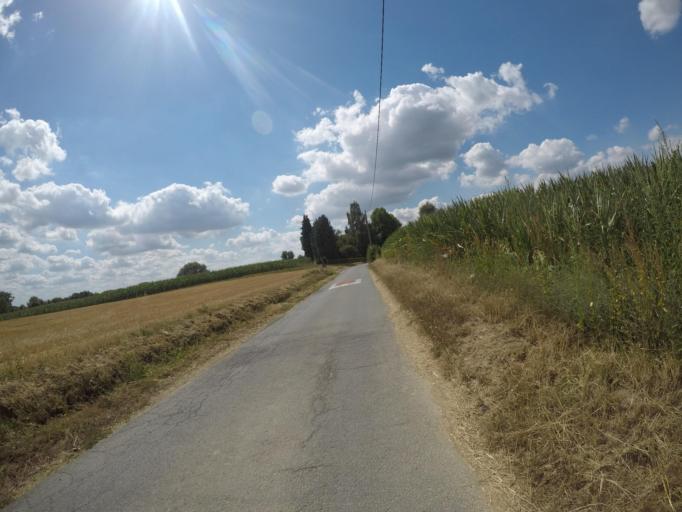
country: BE
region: Flanders
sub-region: Provincie Vlaams-Brabant
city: Gooik
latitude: 50.7961
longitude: 4.1318
